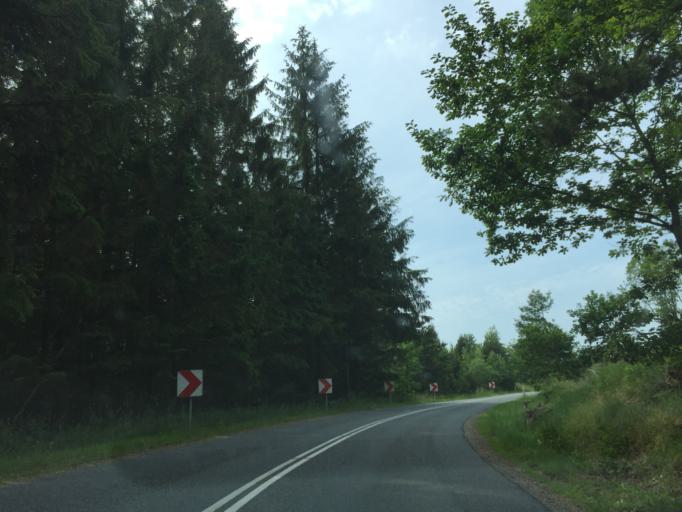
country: DK
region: Central Jutland
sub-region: Silkeborg Kommune
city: Virklund
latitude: 56.1005
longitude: 9.4698
